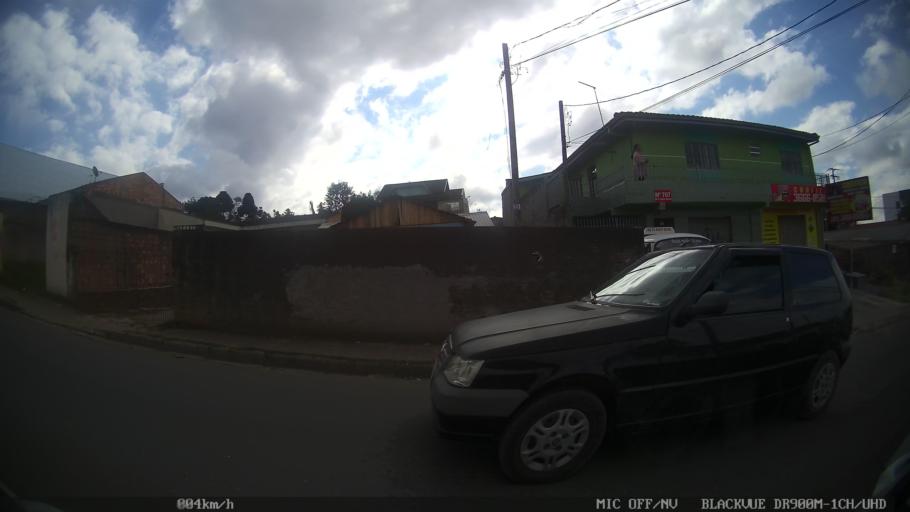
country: BR
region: Parana
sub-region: Colombo
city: Colombo
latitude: -25.3503
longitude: -49.1937
